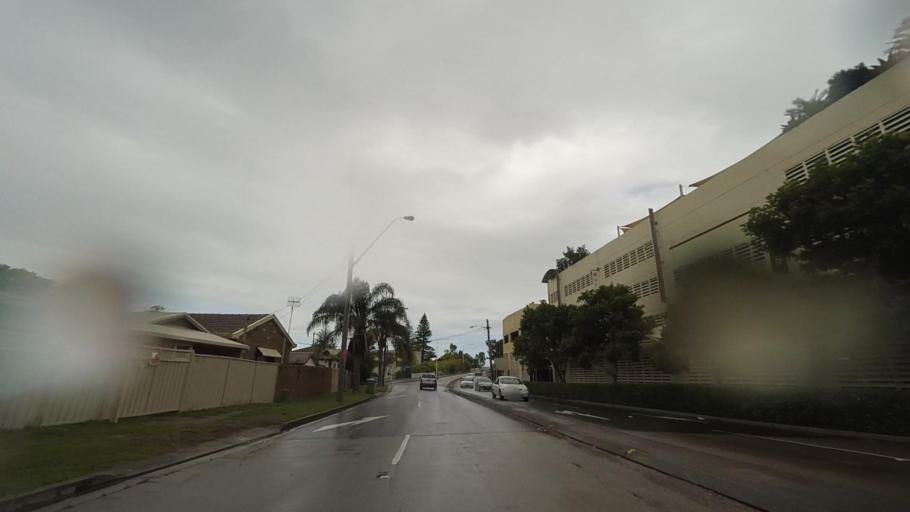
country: AU
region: New South Wales
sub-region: Wyong Shire
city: The Entrance
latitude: -33.3404
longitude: 151.4971
